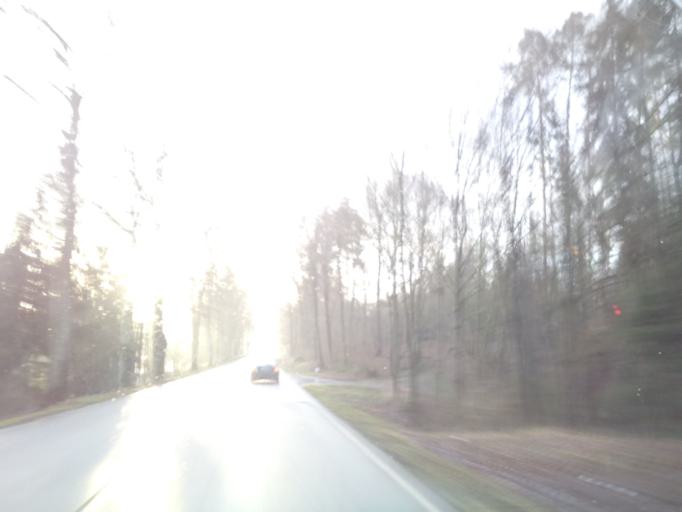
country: DE
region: Bavaria
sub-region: Upper Franconia
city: Lichtenfels
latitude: 50.1631
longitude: 11.0546
